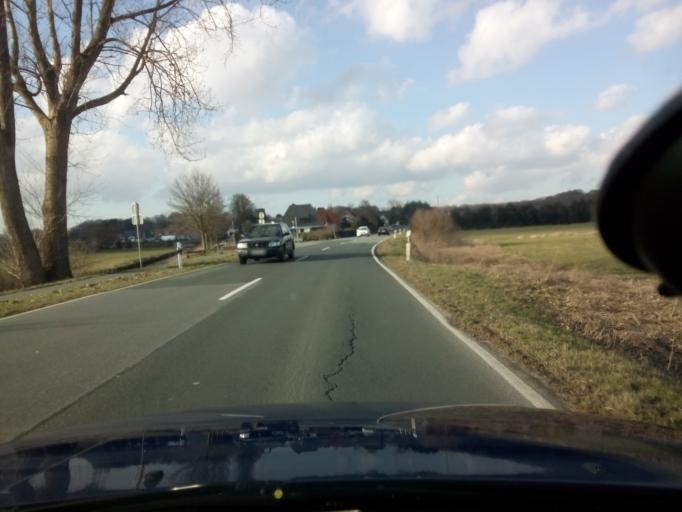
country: DE
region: Lower Saxony
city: Osterholz-Scharmbeck
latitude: 53.2165
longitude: 8.8097
